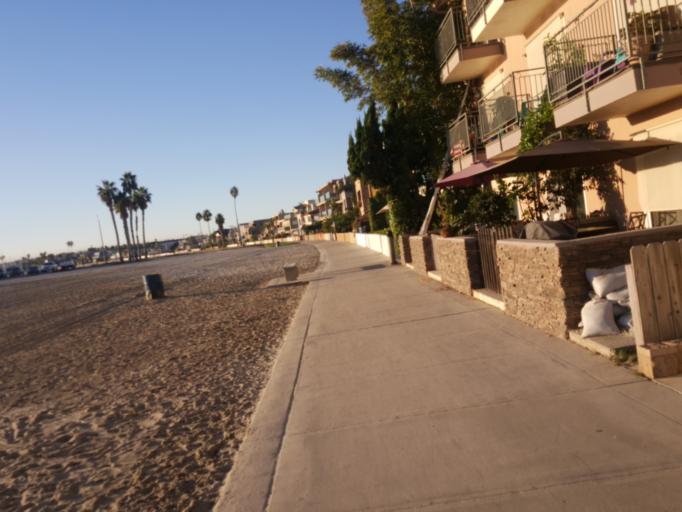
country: US
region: California
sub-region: San Diego County
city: La Jolla
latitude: 32.7797
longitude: -117.2517
